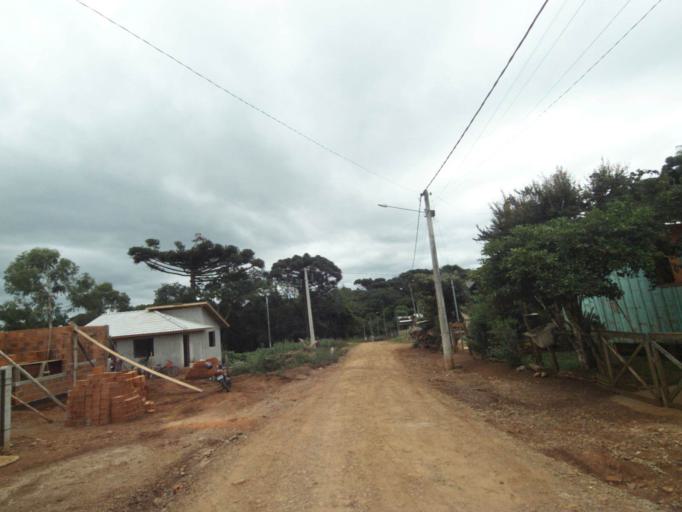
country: BR
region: Rio Grande do Sul
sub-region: Lagoa Vermelha
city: Lagoa Vermelha
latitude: -28.1948
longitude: -51.5289
